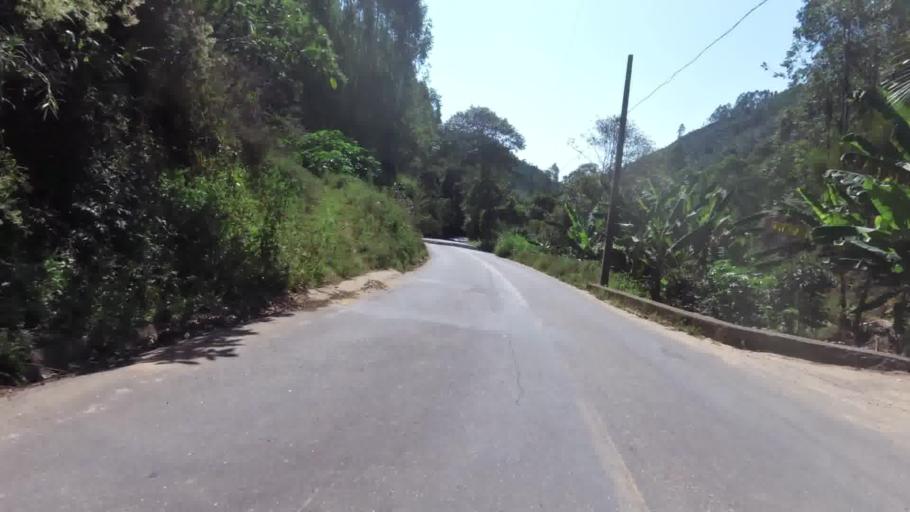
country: BR
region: Espirito Santo
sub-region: Marechal Floriano
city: Marechal Floriano
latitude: -20.4543
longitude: -40.8947
